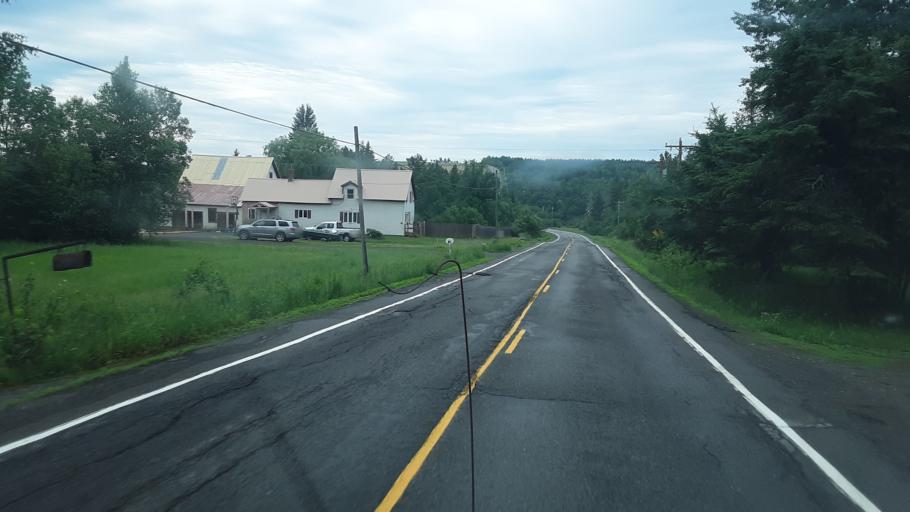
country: US
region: Maine
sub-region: Penobscot County
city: Patten
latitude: 46.0574
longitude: -68.4407
